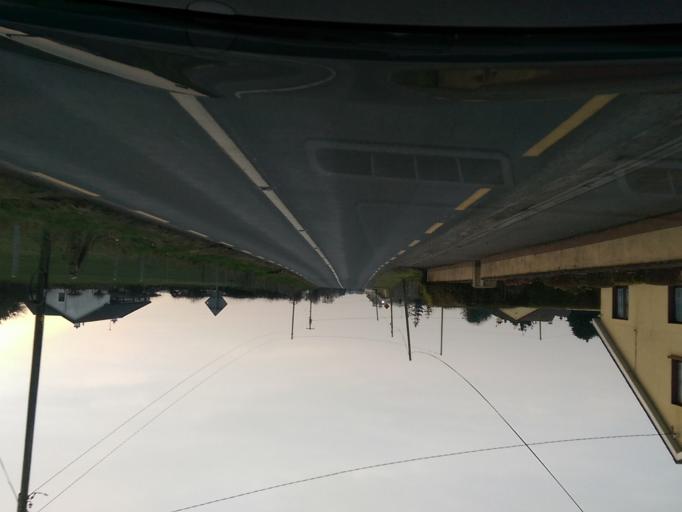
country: IE
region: Leinster
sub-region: An Longfort
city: Ballymahon
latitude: 53.5154
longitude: -7.8218
